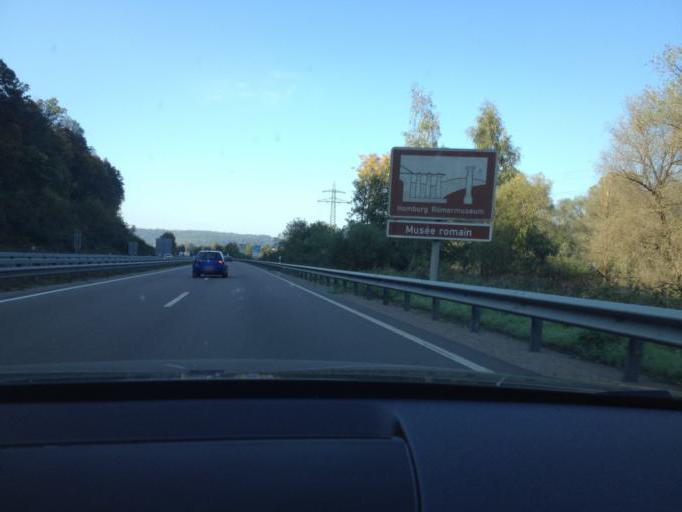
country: DE
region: Rheinland-Pfalz
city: Zweibrucken
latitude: 49.2558
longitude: 7.3305
